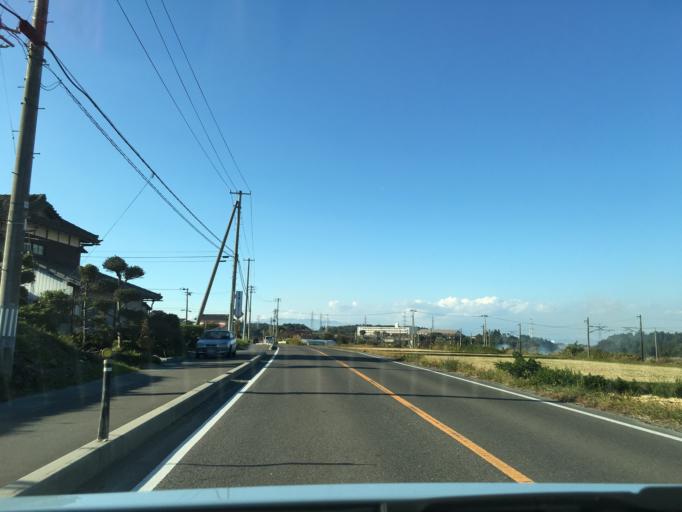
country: JP
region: Fukushima
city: Sukagawa
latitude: 37.3238
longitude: 140.3757
